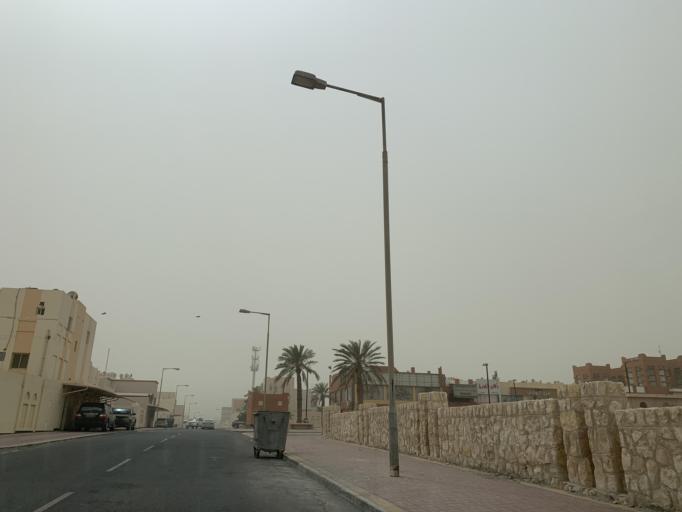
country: BH
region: Central Governorate
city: Madinat Hamad
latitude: 26.1299
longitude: 50.5140
